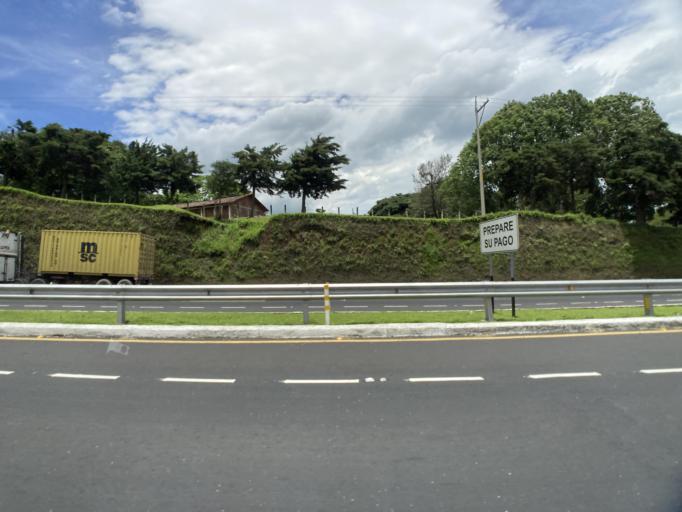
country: GT
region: Escuintla
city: Palin
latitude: 14.4099
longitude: -90.6989
